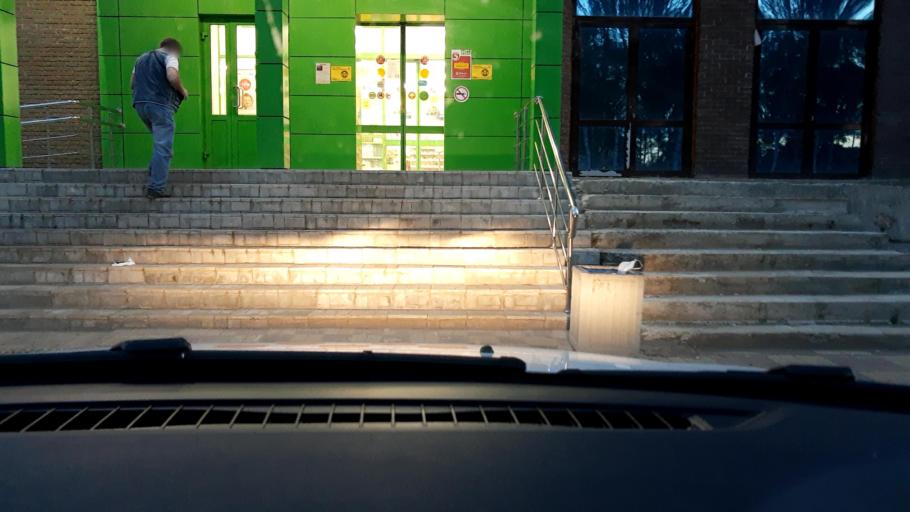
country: RU
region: Nizjnij Novgorod
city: Nizhniy Novgorod
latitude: 56.2148
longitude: 43.9597
